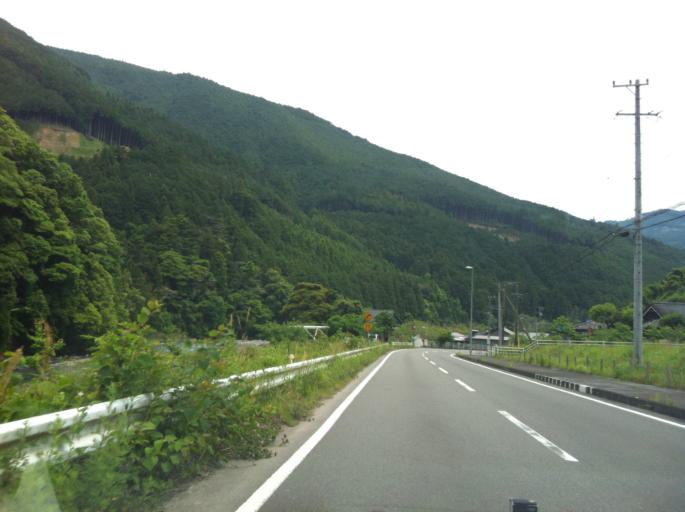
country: JP
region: Shizuoka
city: Shizuoka-shi
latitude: 35.1205
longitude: 138.3261
